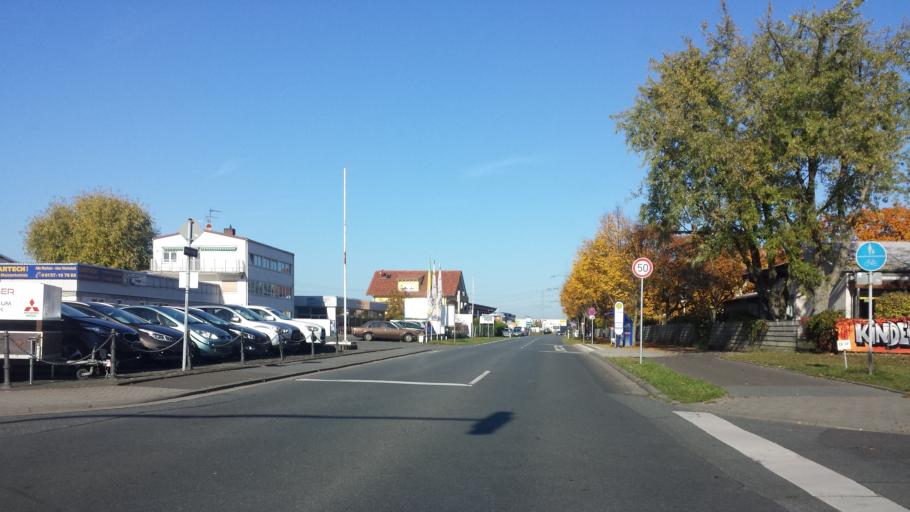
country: DE
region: Hesse
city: Pfungstadt
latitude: 49.8059
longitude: 8.5929
